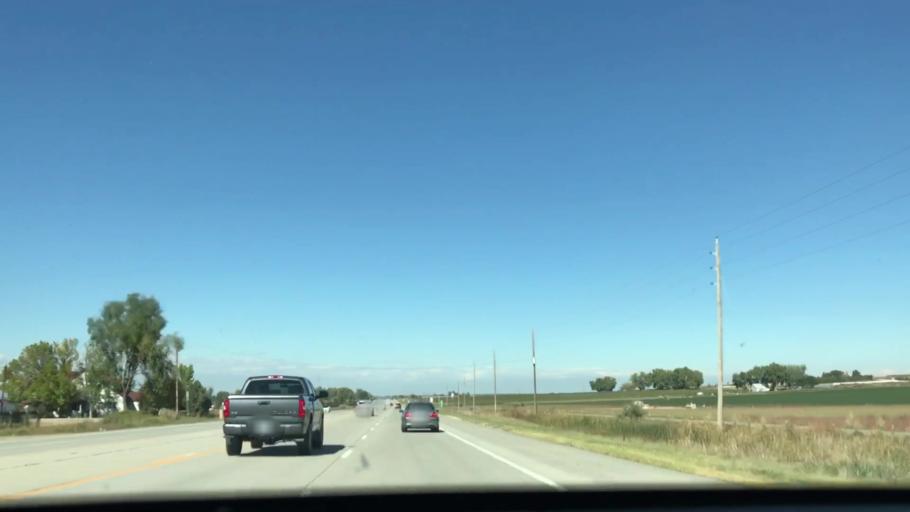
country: US
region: Colorado
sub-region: Boulder County
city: Longmont
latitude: 40.1093
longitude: -105.1035
